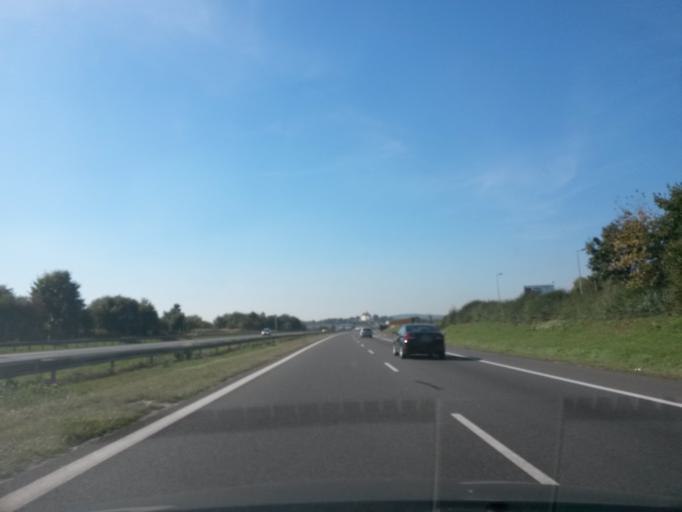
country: PL
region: Lesser Poland Voivodeship
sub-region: Powiat krakowski
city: Balice
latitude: 50.0805
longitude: 19.7717
